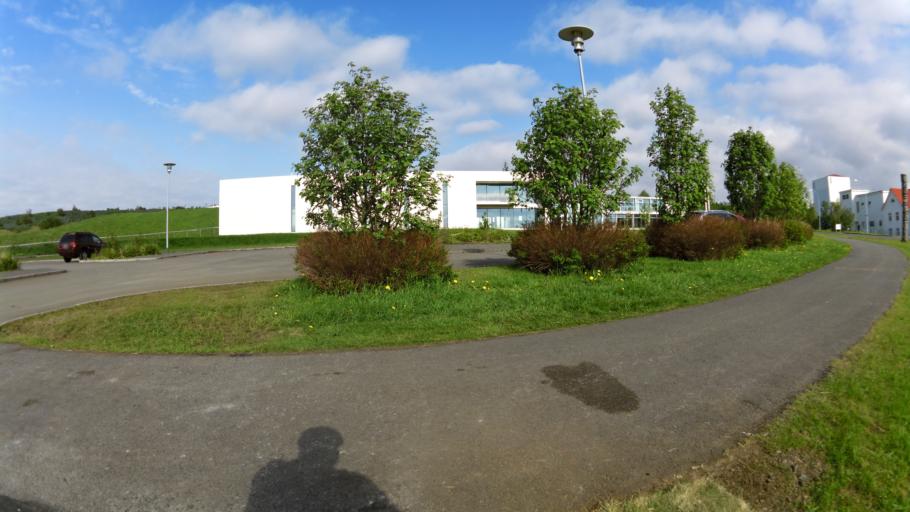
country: IS
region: Capital Region
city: Reykjavik
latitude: 64.1199
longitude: -21.8384
